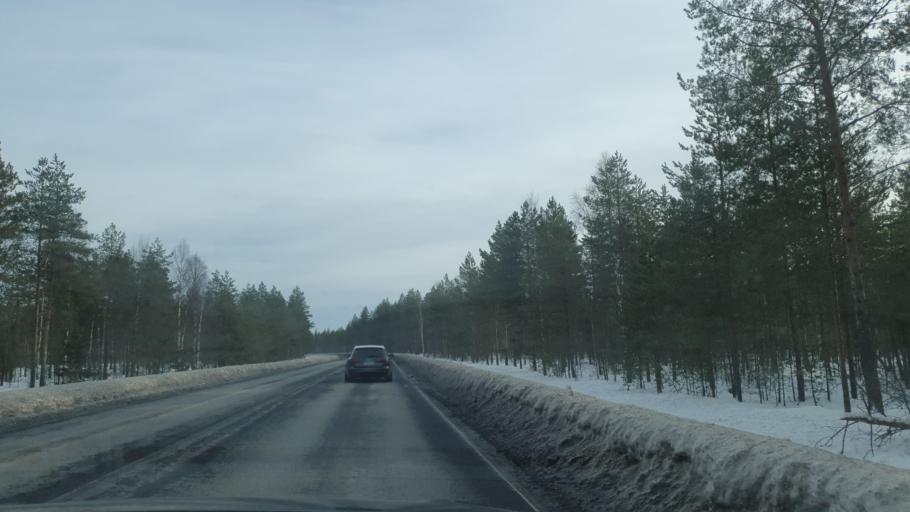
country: FI
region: Northern Ostrobothnia
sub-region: Oulunkaari
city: Utajaervi
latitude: 64.7759
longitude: 26.3030
